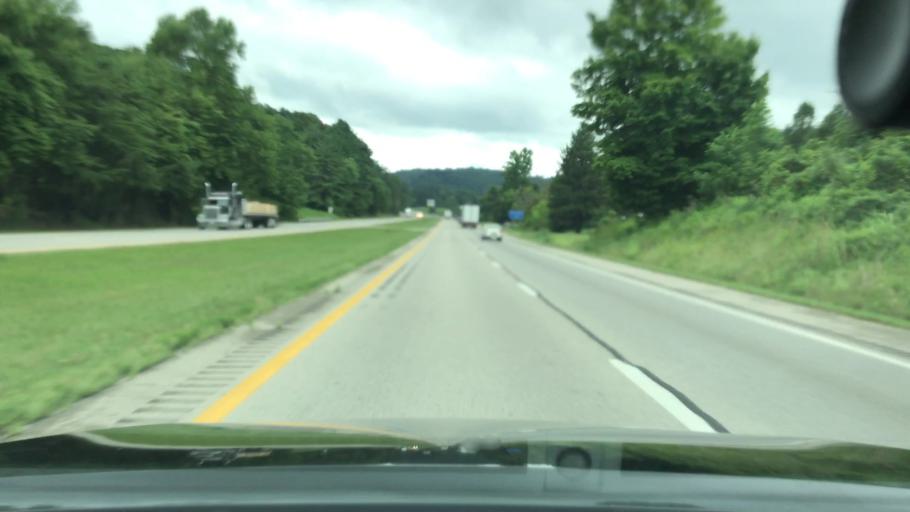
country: US
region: Ohio
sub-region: Jackson County
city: Jackson
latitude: 39.1787
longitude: -82.7495
